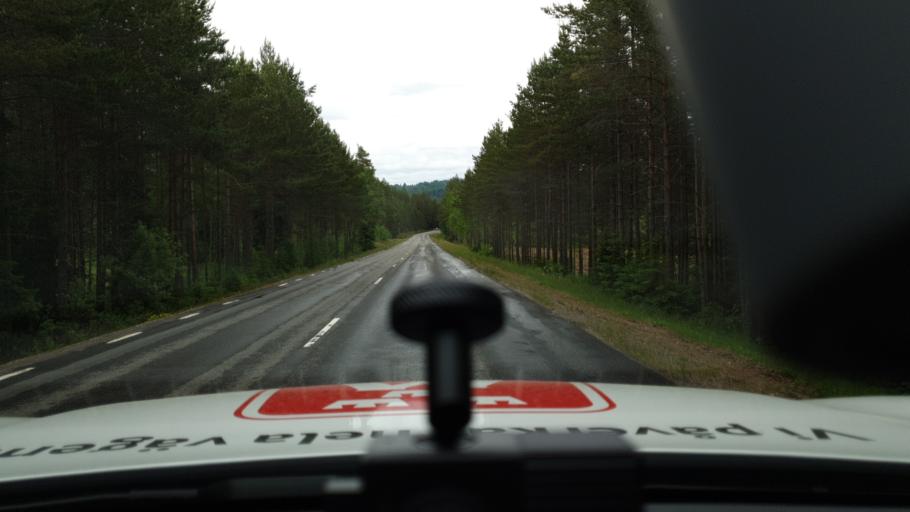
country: SE
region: Joenkoeping
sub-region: Mullsjo Kommun
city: Mullsjoe
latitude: 57.9831
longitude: 13.8194
